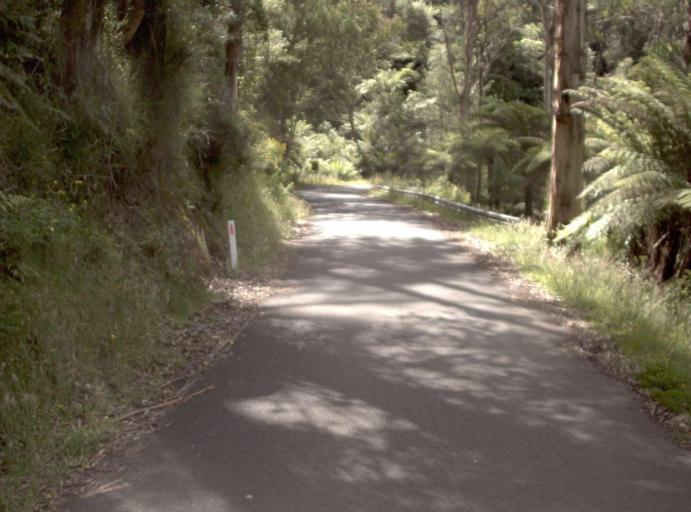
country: AU
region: Victoria
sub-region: Latrobe
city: Moe
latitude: -37.8308
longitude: 146.1614
